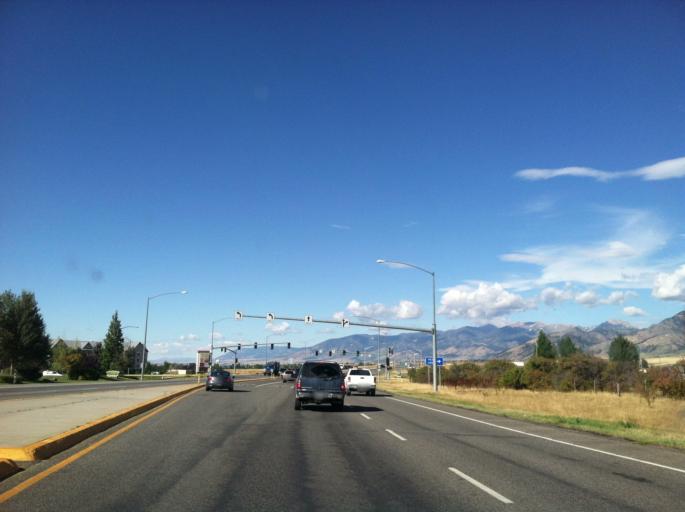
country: US
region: Montana
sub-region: Gallatin County
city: Bozeman
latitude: 45.7105
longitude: -111.0654
